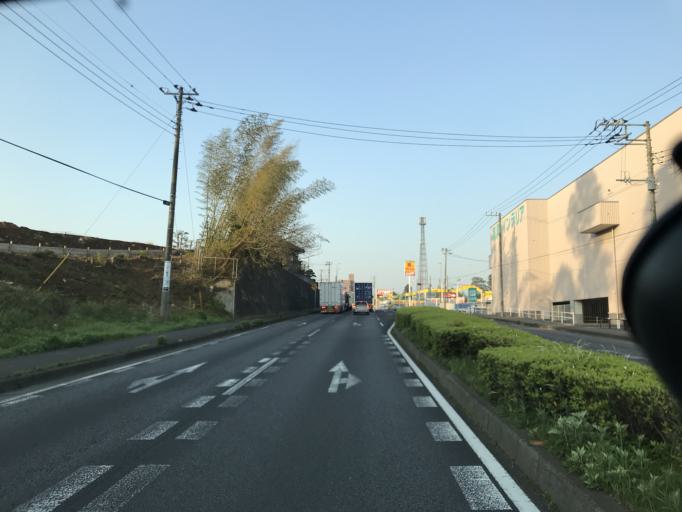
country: JP
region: Chiba
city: Narita
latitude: 35.7690
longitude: 140.3116
